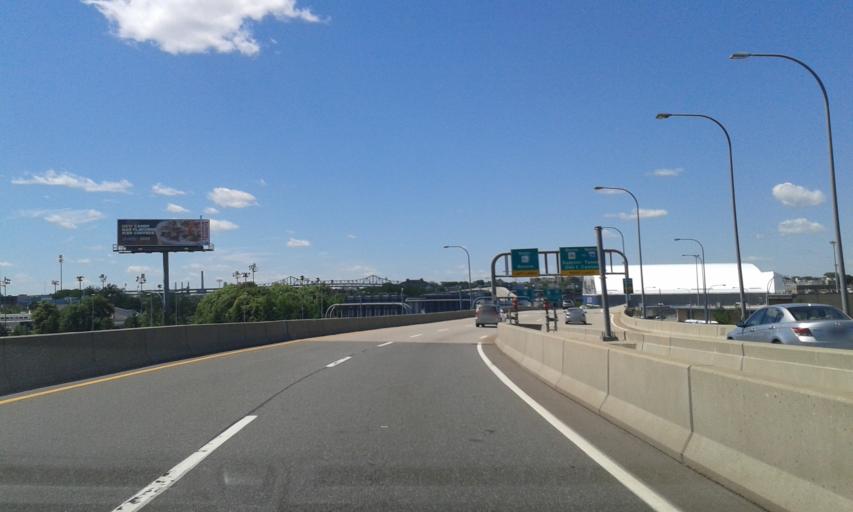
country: US
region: Massachusetts
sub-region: Suffolk County
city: Chelsea
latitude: 42.3693
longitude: -71.0249
